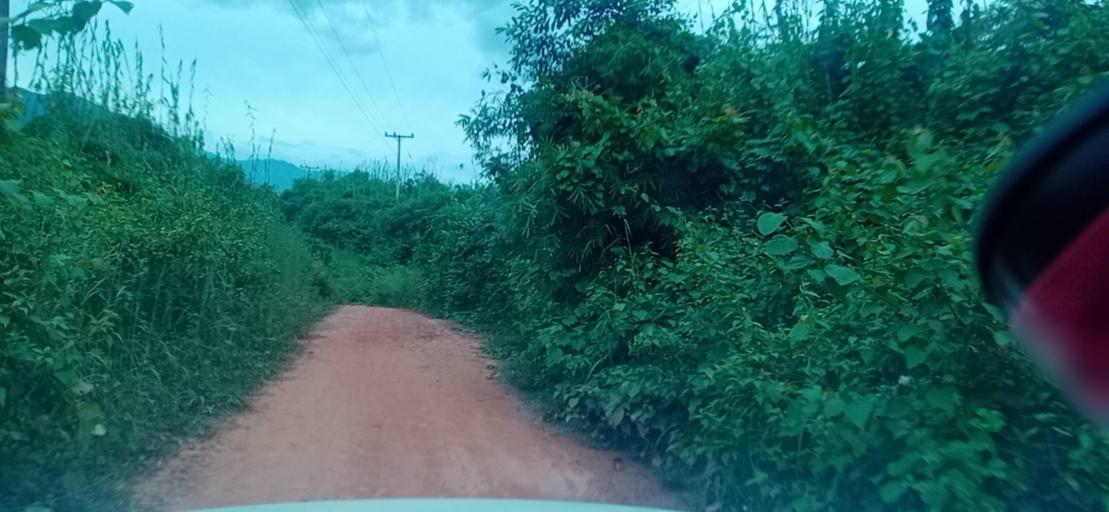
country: TH
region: Changwat Bueng Kan
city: Pak Khat
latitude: 18.5628
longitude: 103.3018
